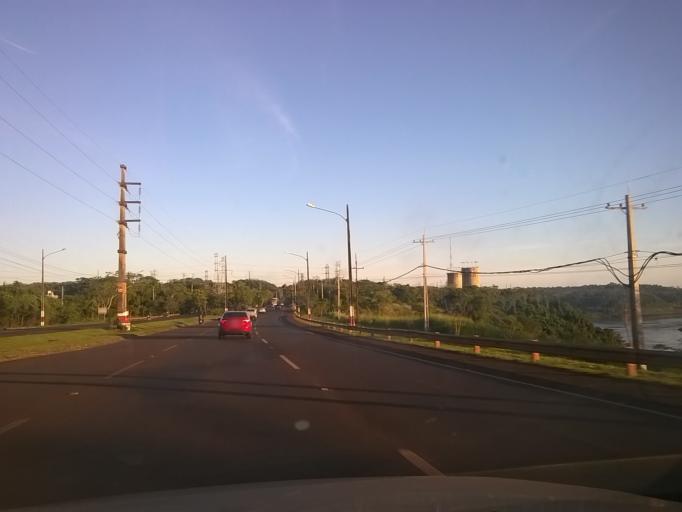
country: PY
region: Alto Parana
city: Ciudad del Este
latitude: -25.4652
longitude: -54.6242
